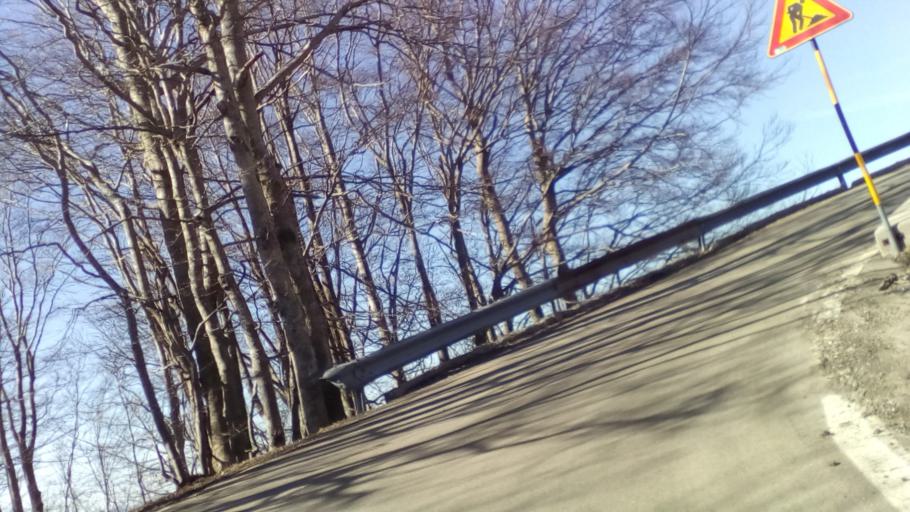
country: IT
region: Tuscany
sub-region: Provincia di Lucca
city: Fosciandora
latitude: 44.1873
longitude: 10.4797
